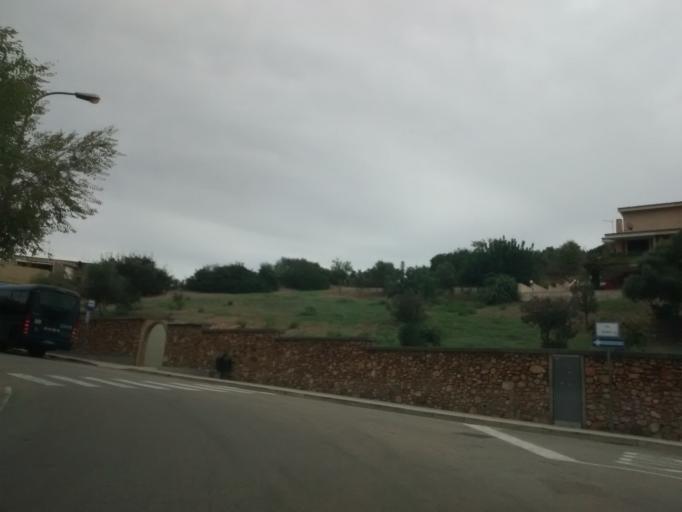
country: IT
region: Sardinia
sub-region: Provincia di Cagliari
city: Villasimius
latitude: 39.1440
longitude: 9.5151
